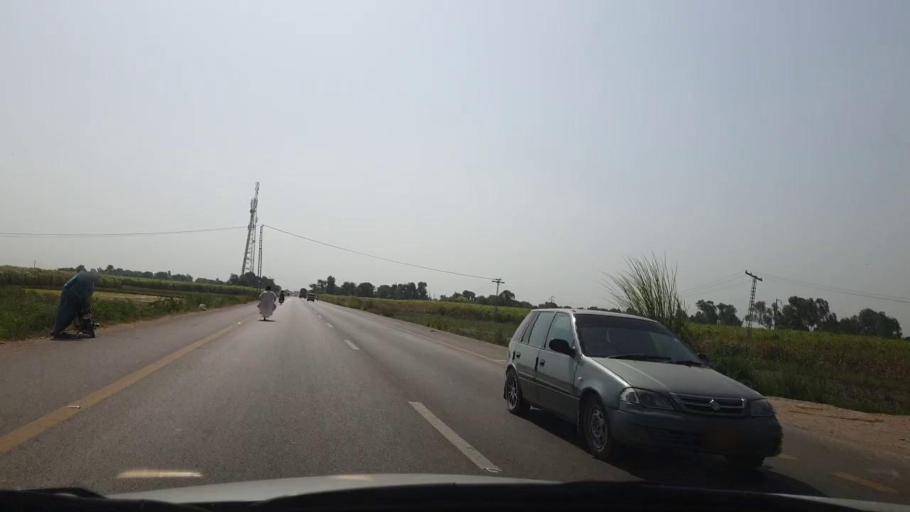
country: PK
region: Sindh
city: Tando Muhammad Khan
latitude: 25.0921
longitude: 68.5986
